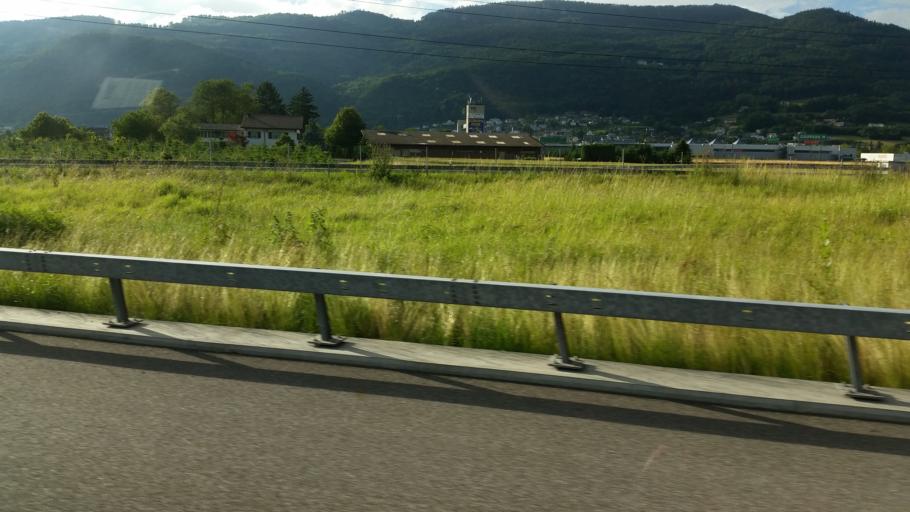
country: CH
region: Solothurn
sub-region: Bezirk Gaeu
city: Egerkingen
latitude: 47.3120
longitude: 7.8045
